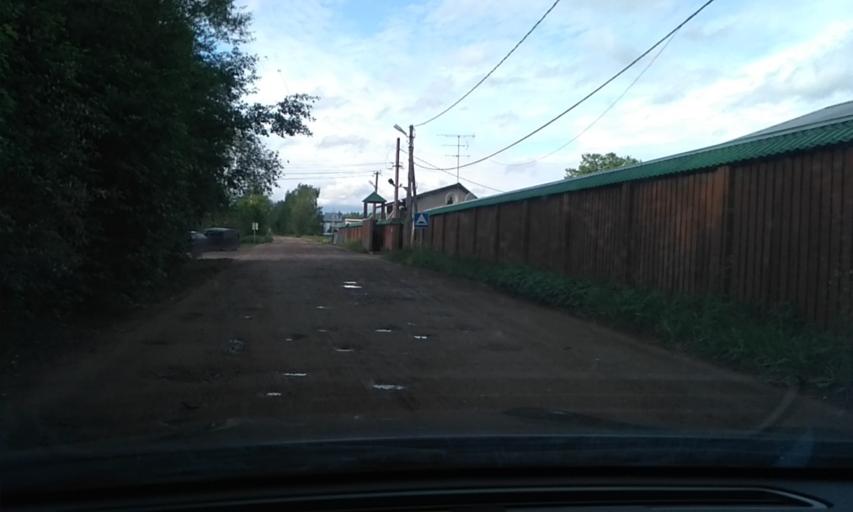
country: RU
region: Leningrad
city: Otradnoye
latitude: 59.7994
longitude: 30.8012
